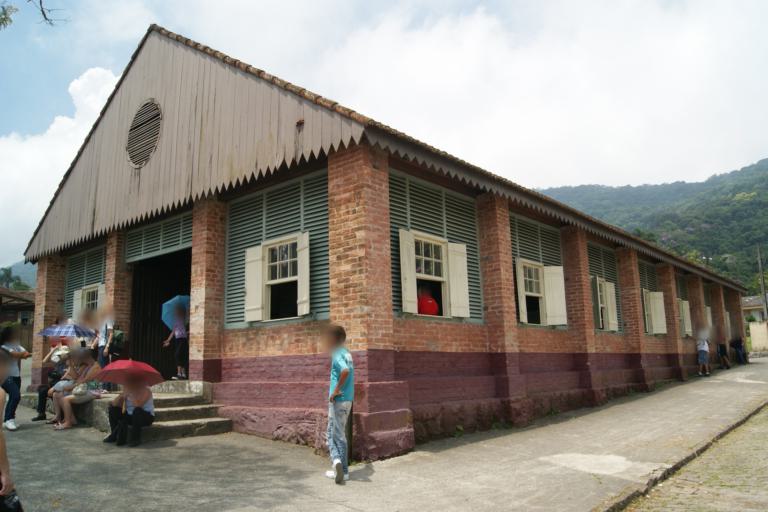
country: BR
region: Sao Paulo
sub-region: Rio Grande Da Serra
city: Rio Grande da Serra
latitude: -23.7775
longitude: -46.3004
